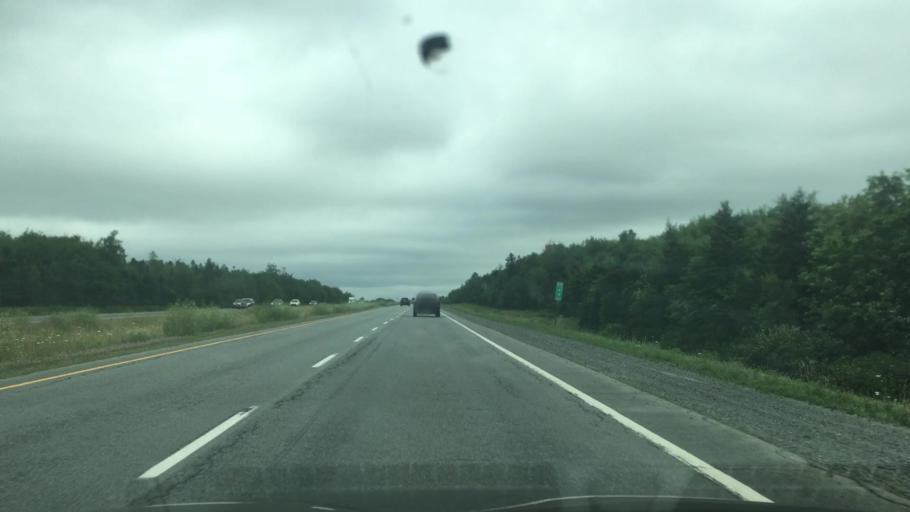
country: CA
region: Nova Scotia
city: Cole Harbour
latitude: 44.9893
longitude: -63.4976
